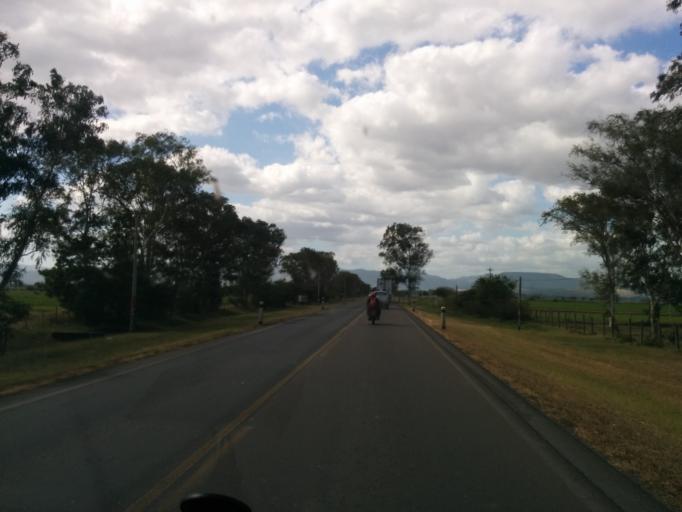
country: NI
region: Matagalpa
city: Ciudad Dario
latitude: 12.8648
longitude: -86.1142
